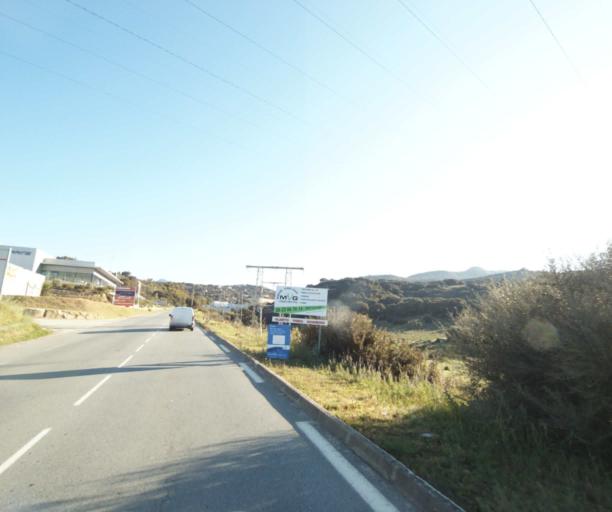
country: FR
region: Corsica
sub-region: Departement de la Corse-du-Sud
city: Propriano
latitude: 41.6619
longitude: 8.9179
